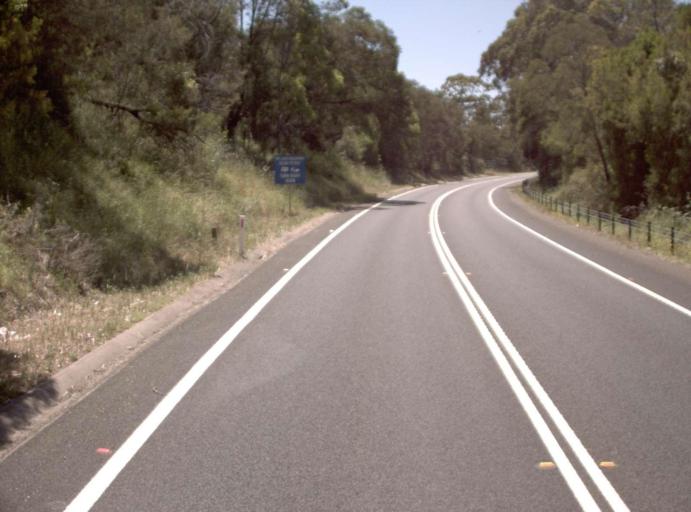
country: AU
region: Victoria
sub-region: East Gippsland
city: Lakes Entrance
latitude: -37.8503
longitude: 148.0381
